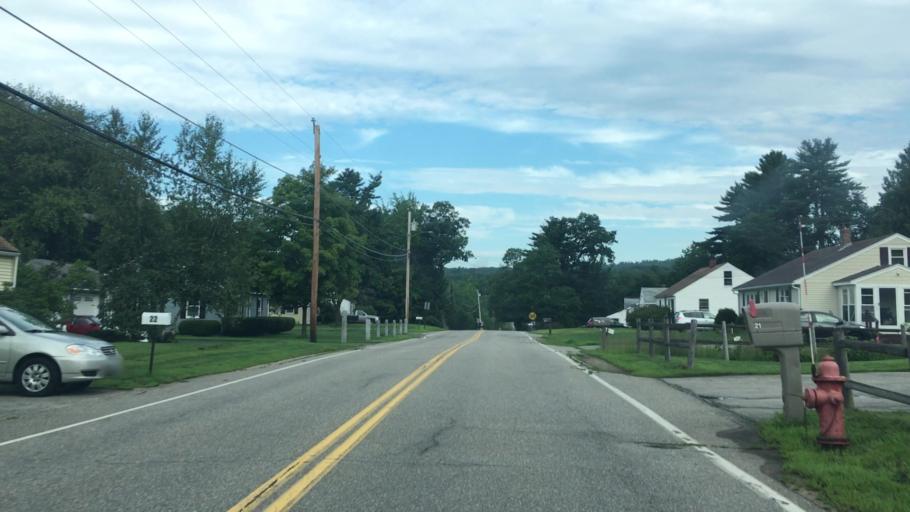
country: US
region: New Hampshire
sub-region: Strafford County
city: Rochester
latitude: 43.3494
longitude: -70.9780
